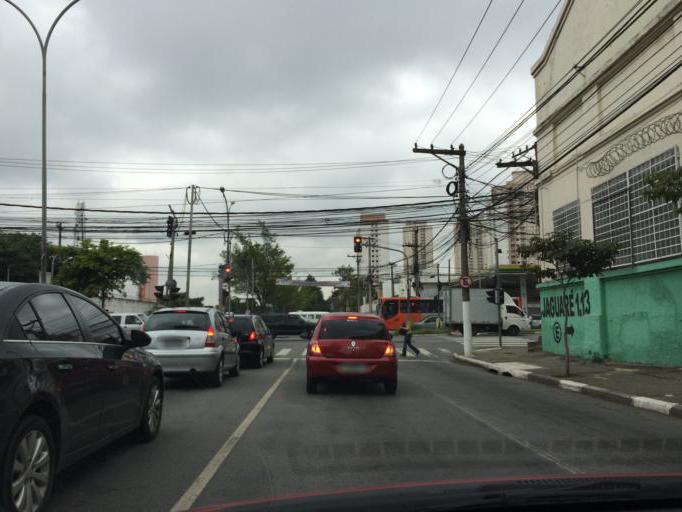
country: BR
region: Sao Paulo
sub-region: Osasco
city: Osasco
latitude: -23.5509
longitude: -46.7405
